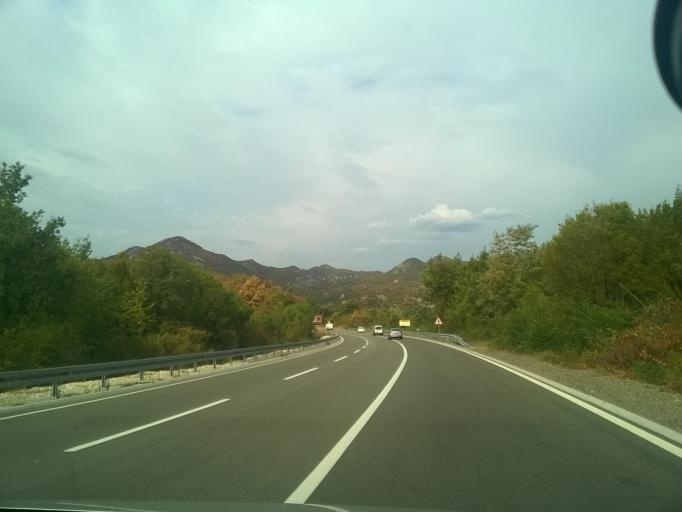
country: ME
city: Mojanovici
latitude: 42.3872
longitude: 19.0734
